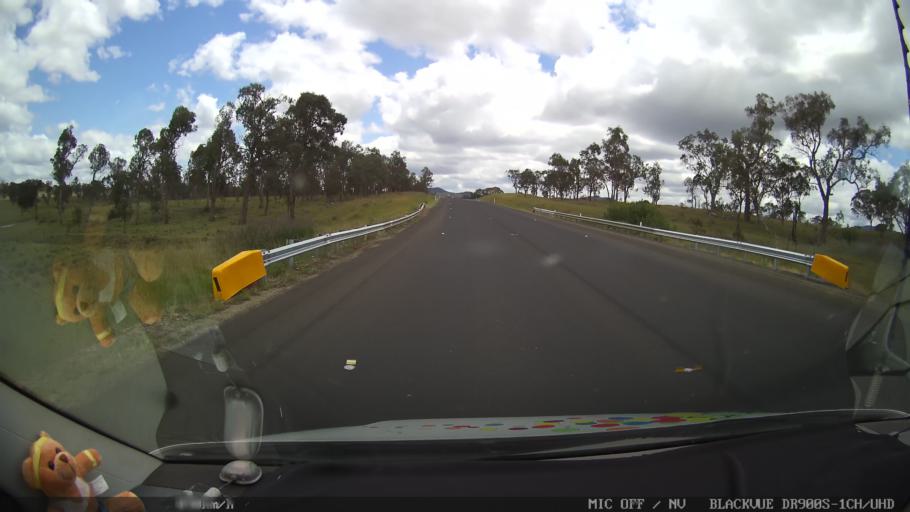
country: AU
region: New South Wales
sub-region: Glen Innes Severn
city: Glen Innes
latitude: -29.3872
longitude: 151.8898
